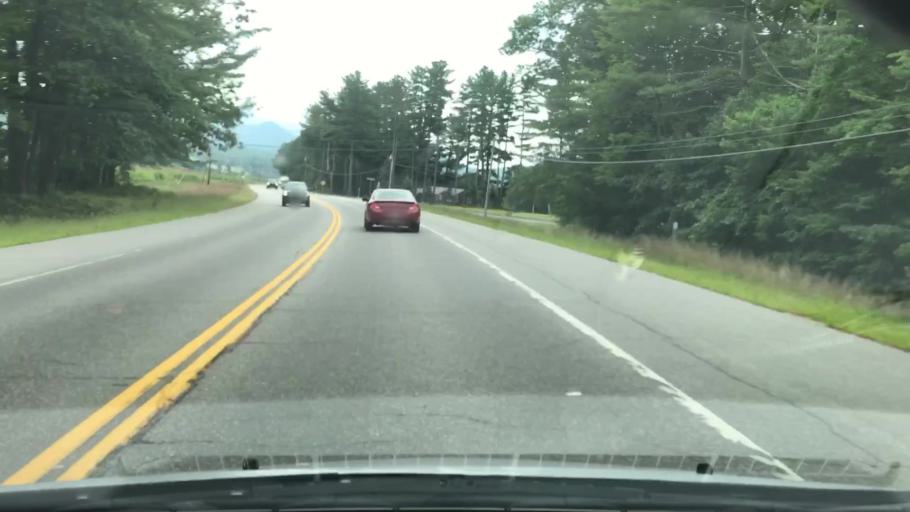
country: US
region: New Hampshire
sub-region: Grafton County
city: North Haverhill
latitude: 44.1065
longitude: -72.0365
